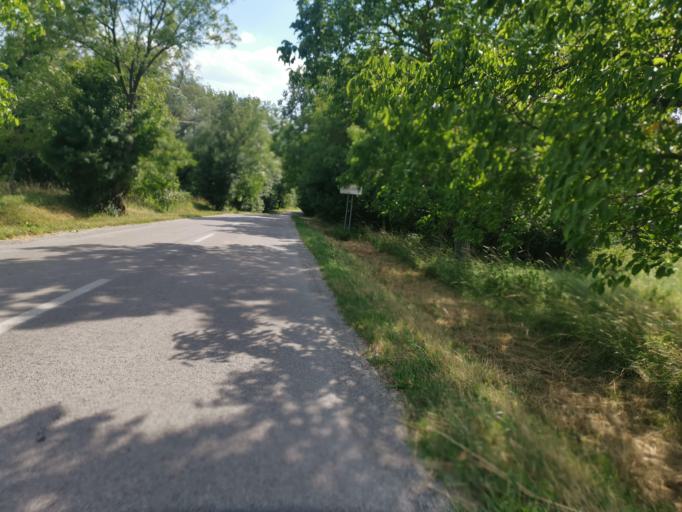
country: CZ
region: South Moravian
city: Knezdub
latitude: 48.8047
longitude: 17.4175
